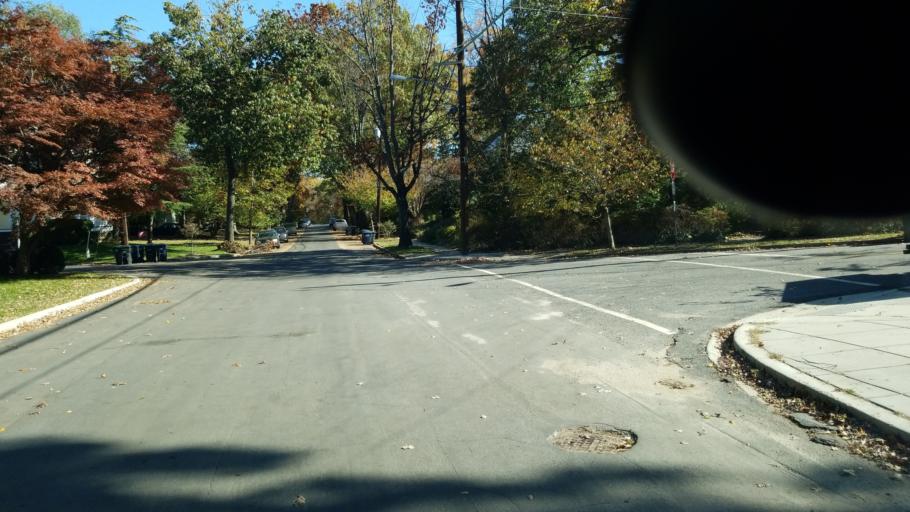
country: US
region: Maryland
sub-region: Montgomery County
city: Chevy Chase
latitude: 38.9728
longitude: -77.0584
